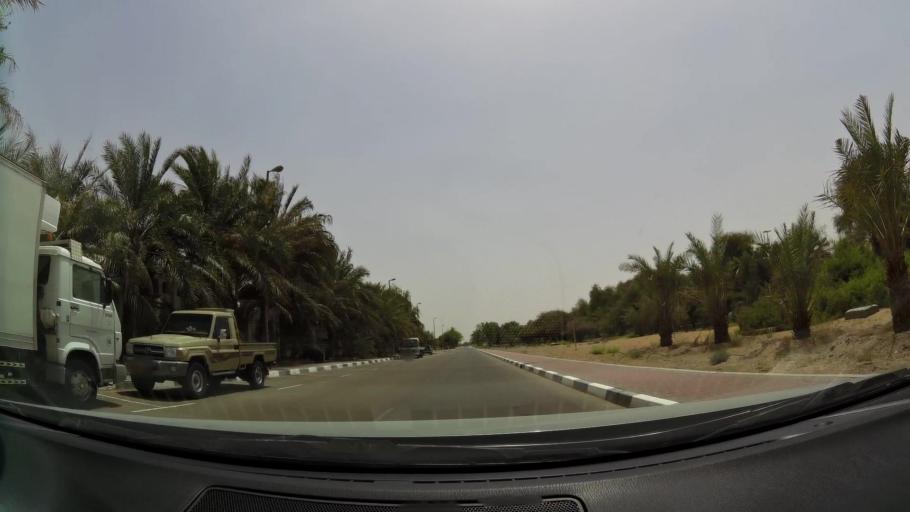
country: AE
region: Abu Dhabi
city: Al Ain
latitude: 24.1905
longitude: 55.6745
